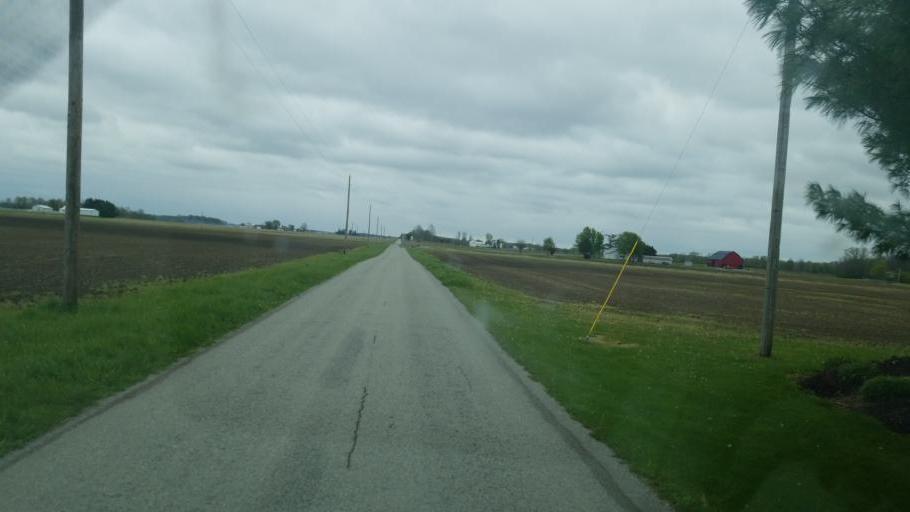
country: US
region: Ohio
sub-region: Hardin County
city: Kenton
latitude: 40.7213
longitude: -83.5950
